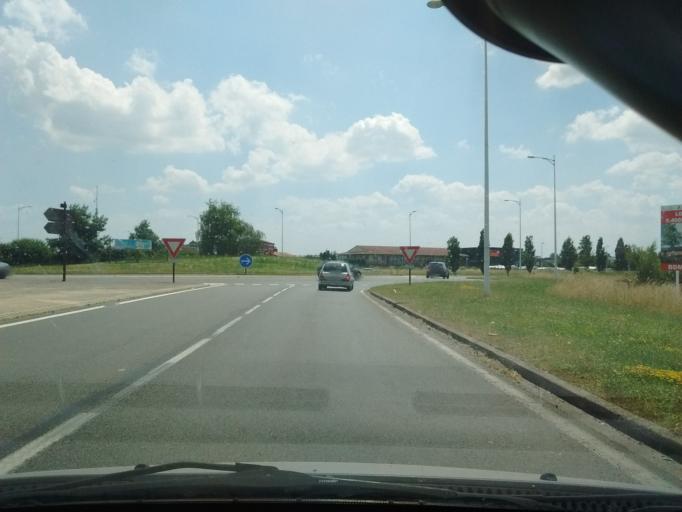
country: FR
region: Ile-de-France
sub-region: Departement de Seine-et-Marne
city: Saint-Fargeau-Ponthierry
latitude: 48.5396
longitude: 2.5186
